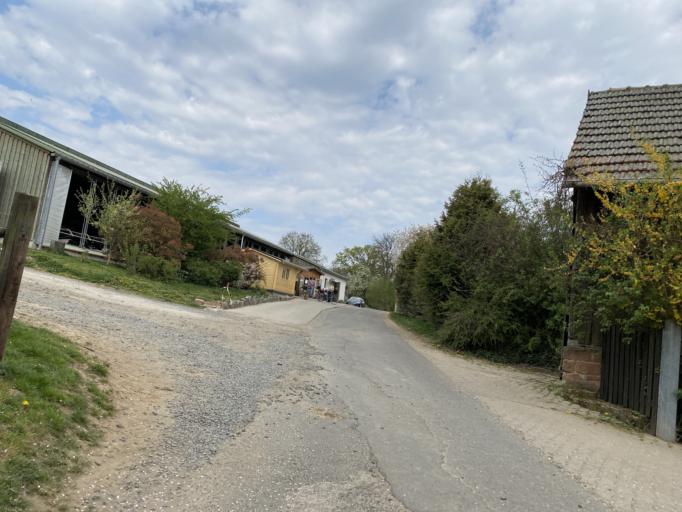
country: DE
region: Hesse
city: Budingen
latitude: 50.2545
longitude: 9.0714
